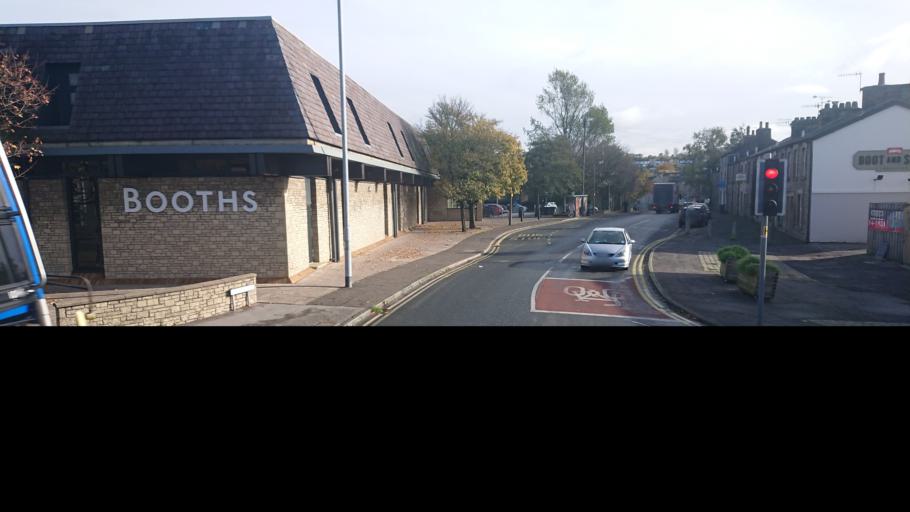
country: GB
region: England
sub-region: Lancashire
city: Lancaster
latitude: 54.0278
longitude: -2.7953
